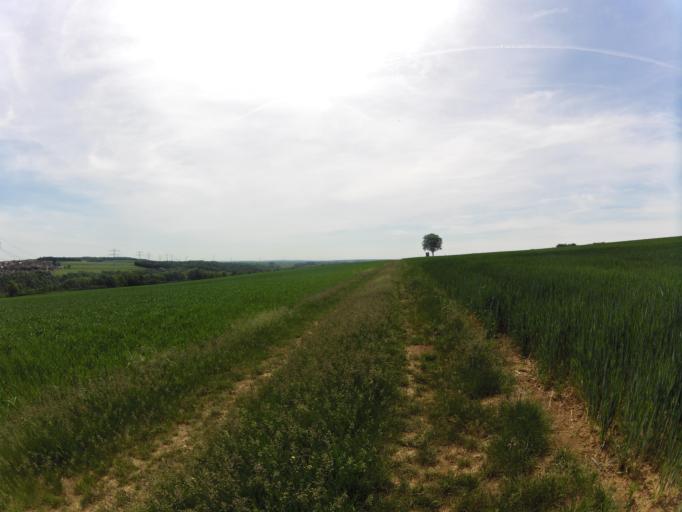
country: DE
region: Bavaria
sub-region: Regierungsbezirk Unterfranken
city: Ochsenfurt
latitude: 49.6657
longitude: 10.0322
